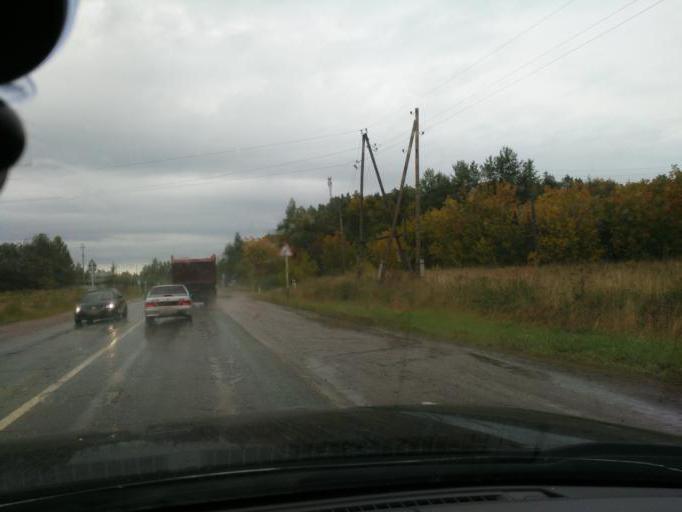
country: RU
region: Perm
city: Kultayevo
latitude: 57.8386
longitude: 55.8229
